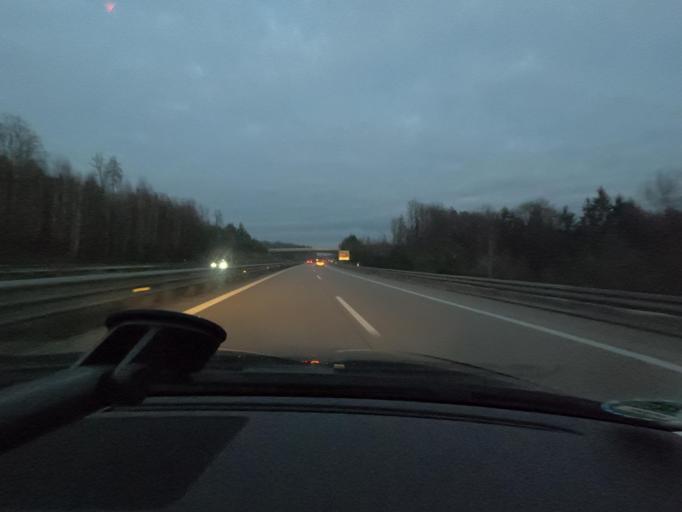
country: DE
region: Bavaria
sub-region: Upper Franconia
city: Niederfullbach
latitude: 50.1946
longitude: 11.0321
